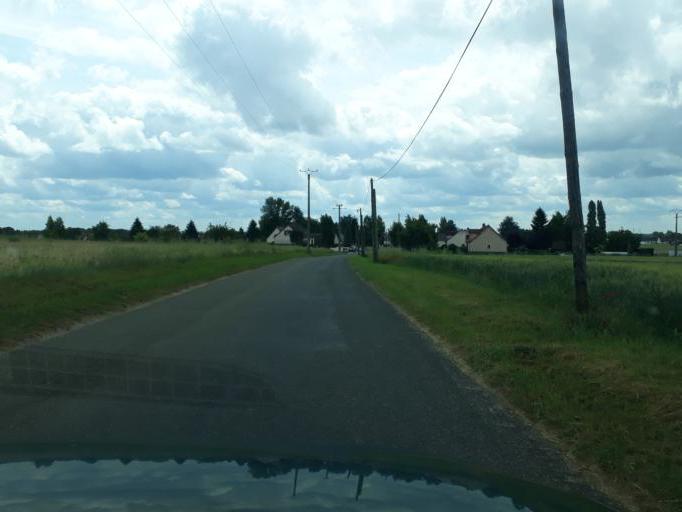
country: FR
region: Centre
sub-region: Departement du Loiret
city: Ingre
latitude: 47.9194
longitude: 1.8074
